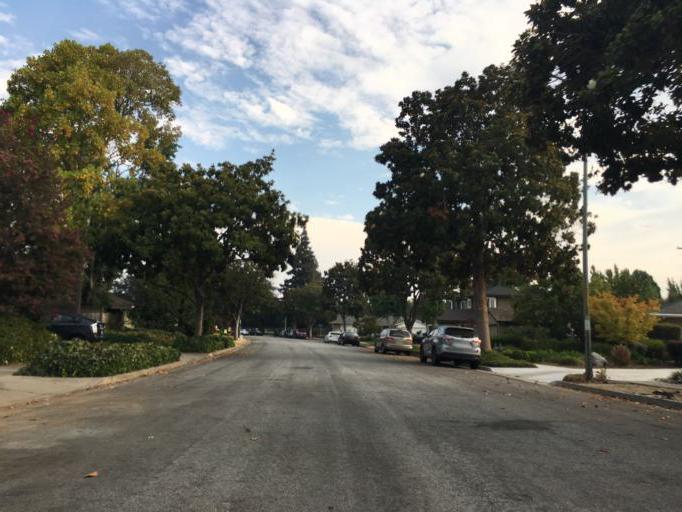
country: US
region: California
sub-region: Santa Clara County
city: Cupertino
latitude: 37.3431
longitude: -122.0633
